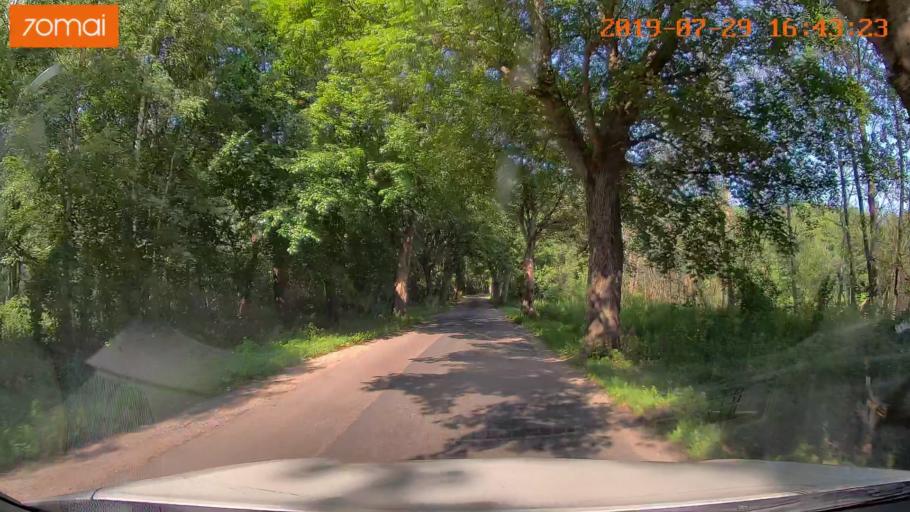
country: RU
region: Kaliningrad
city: Primorsk
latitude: 54.7486
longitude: 20.0837
